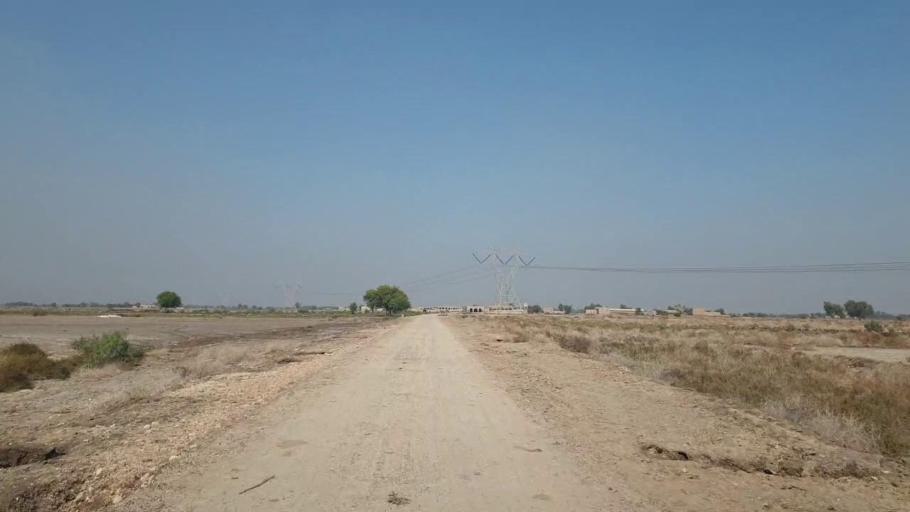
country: PK
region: Sindh
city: Sehwan
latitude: 26.4182
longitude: 67.8105
